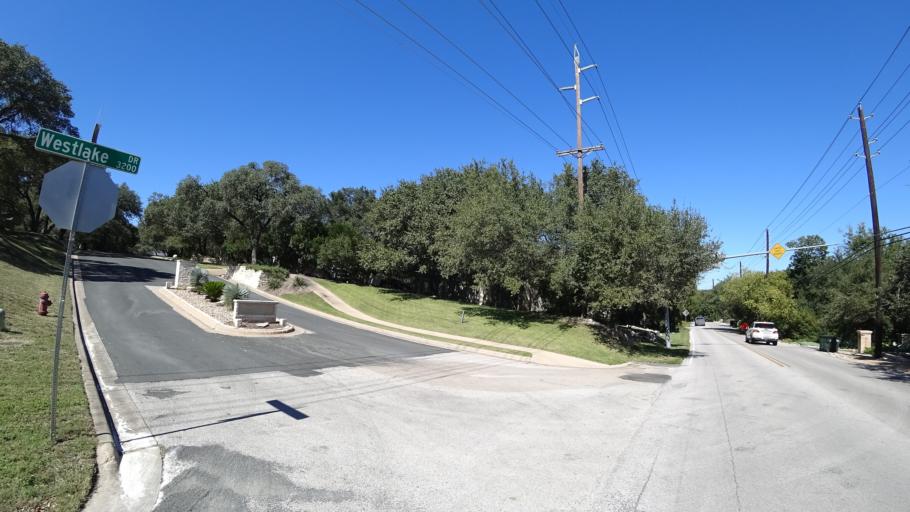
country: US
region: Texas
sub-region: Travis County
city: West Lake Hills
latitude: 30.3192
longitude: -97.7795
